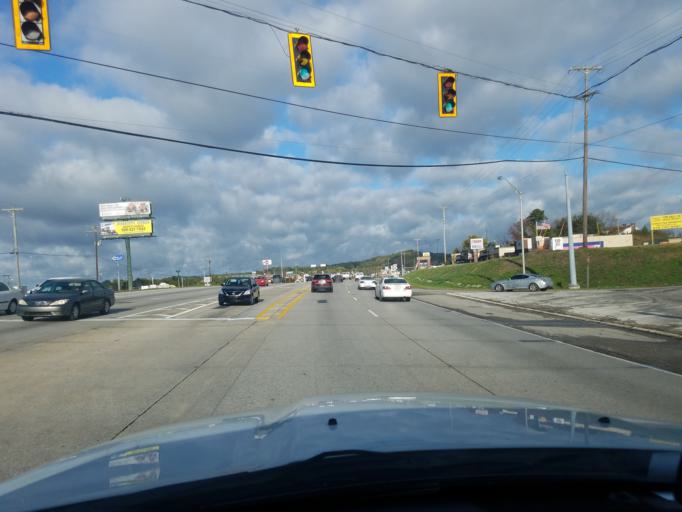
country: US
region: Kentucky
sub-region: Laurel County
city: London
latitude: 37.1064
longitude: -84.0849
